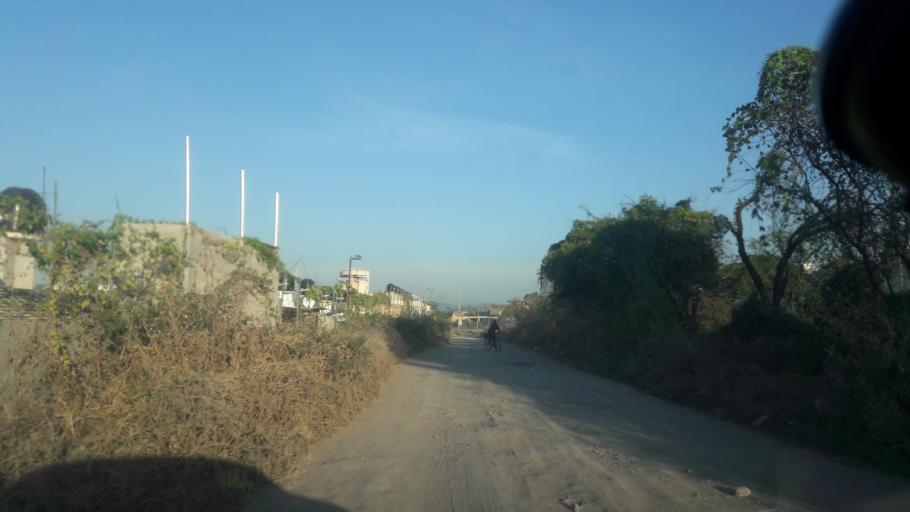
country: MX
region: Guanajuato
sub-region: Leon
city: Medina
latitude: 21.1649
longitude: -101.6345
